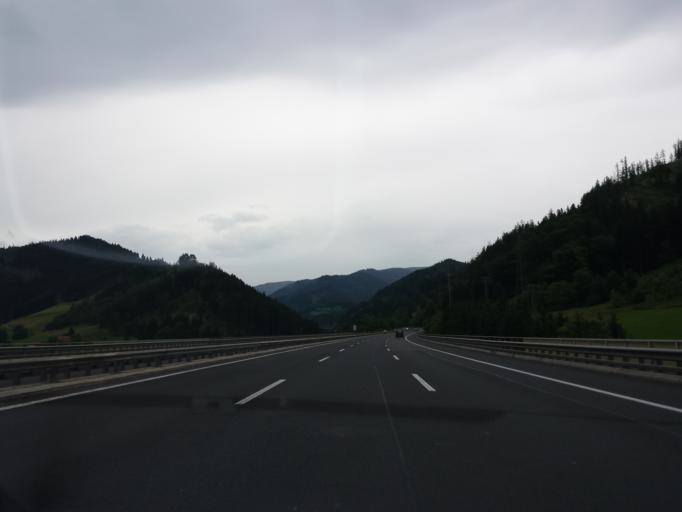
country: AT
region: Styria
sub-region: Politischer Bezirk Graz-Umgebung
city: Ubelbach
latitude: 47.2299
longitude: 15.2172
